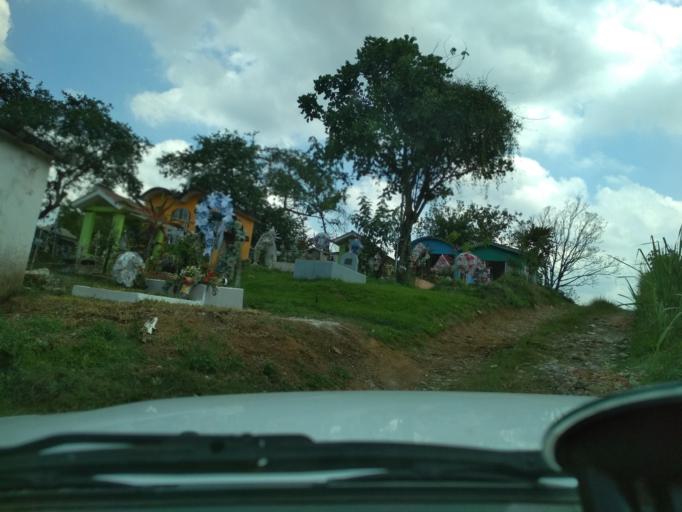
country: MX
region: Veracruz
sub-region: Fortin
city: Monte Salas
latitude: 18.9302
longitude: -97.0163
